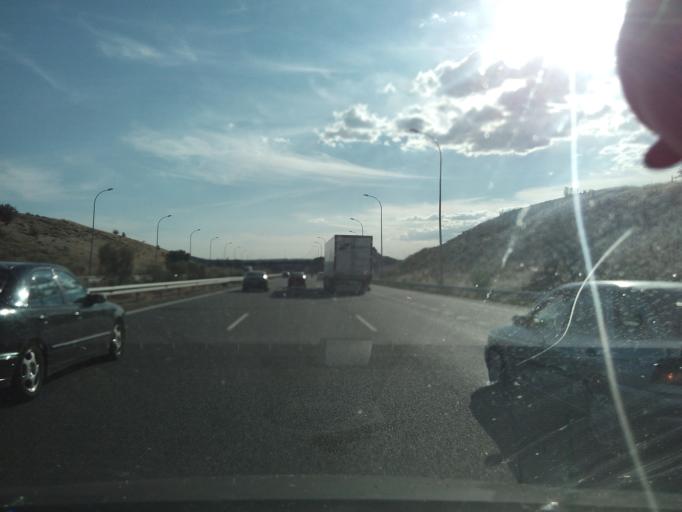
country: ES
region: Madrid
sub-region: Provincia de Madrid
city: Villa de Vallecas
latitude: 40.3367
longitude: -3.6193
